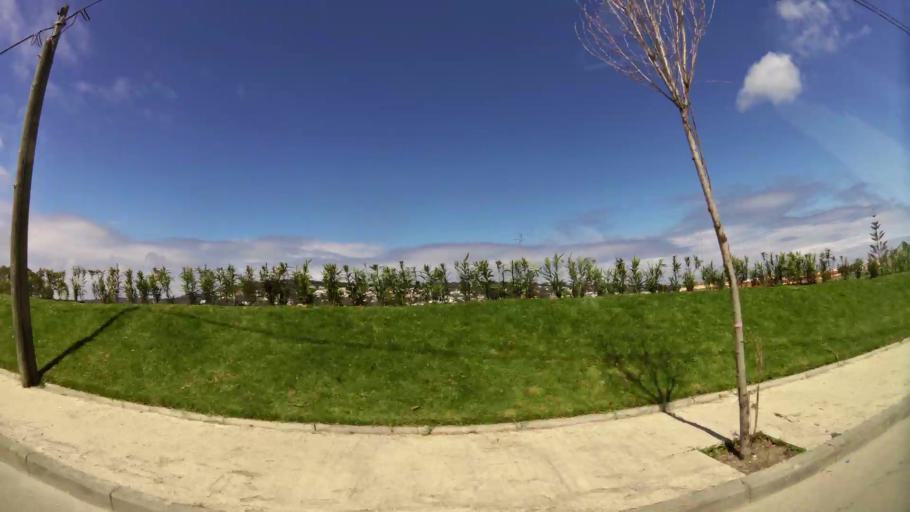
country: MA
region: Tanger-Tetouan
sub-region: Tanger-Assilah
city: Tangier
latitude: 35.7752
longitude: -5.8397
